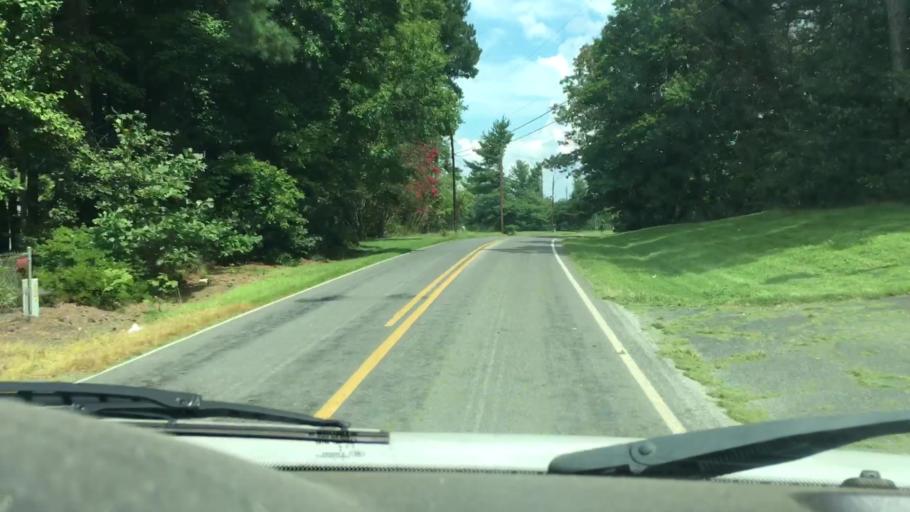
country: US
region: North Carolina
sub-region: Iredell County
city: Mooresville
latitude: 35.6624
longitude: -80.7990
